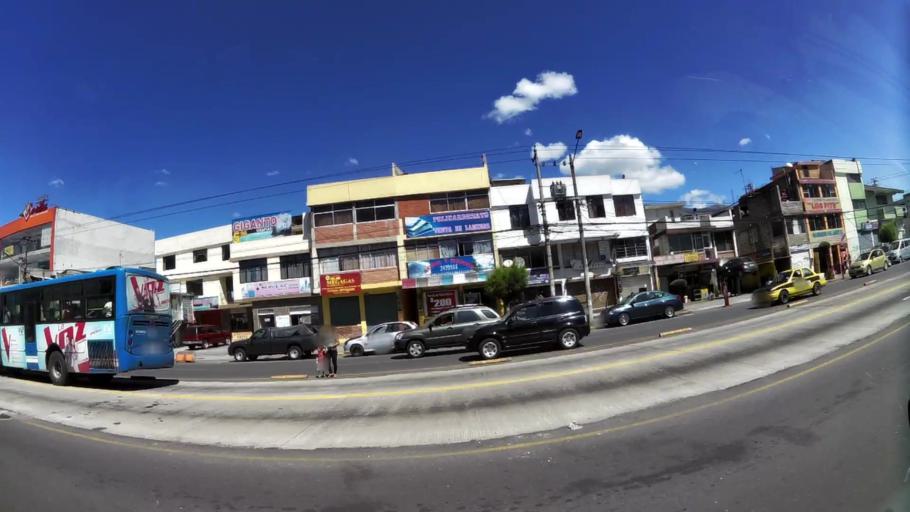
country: EC
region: Pichincha
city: Quito
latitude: -0.1563
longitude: -78.4883
